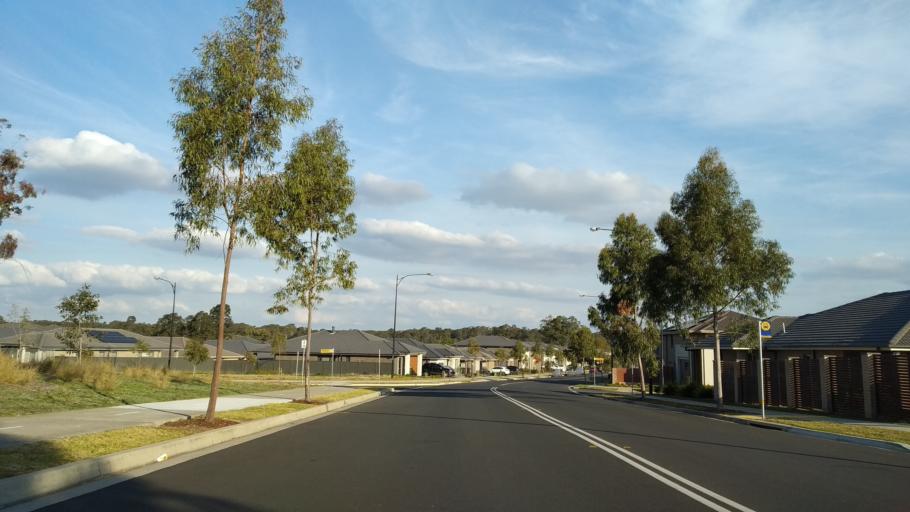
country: AU
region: New South Wales
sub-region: Penrith Municipality
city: Werrington Downs
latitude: -33.7242
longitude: 150.7358
